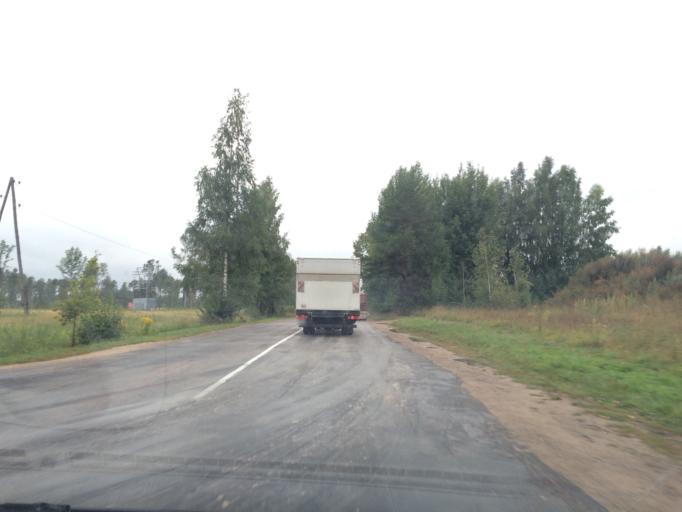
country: LV
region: Ikskile
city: Ikskile
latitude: 56.8550
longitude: 24.5326
